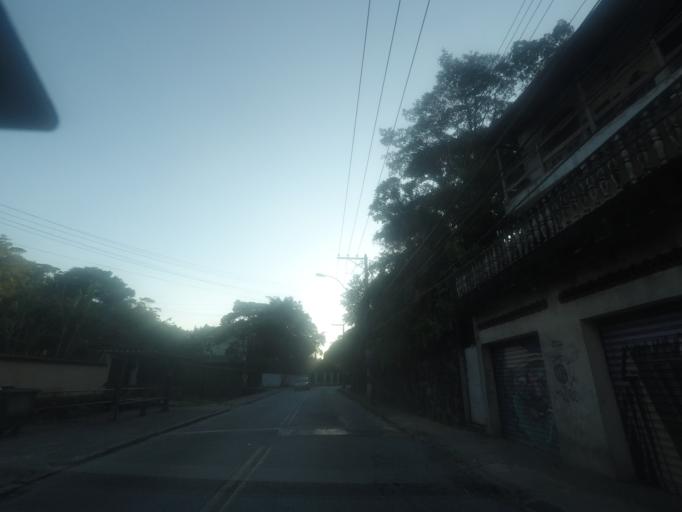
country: BR
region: Rio de Janeiro
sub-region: Petropolis
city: Petropolis
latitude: -22.5274
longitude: -43.1886
